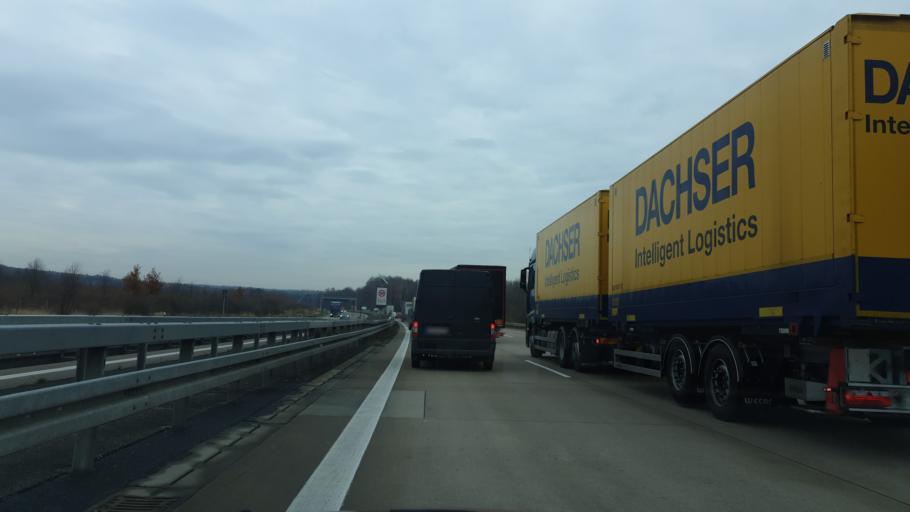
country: DE
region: Saxony
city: Rosswein
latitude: 51.0012
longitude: 13.2094
